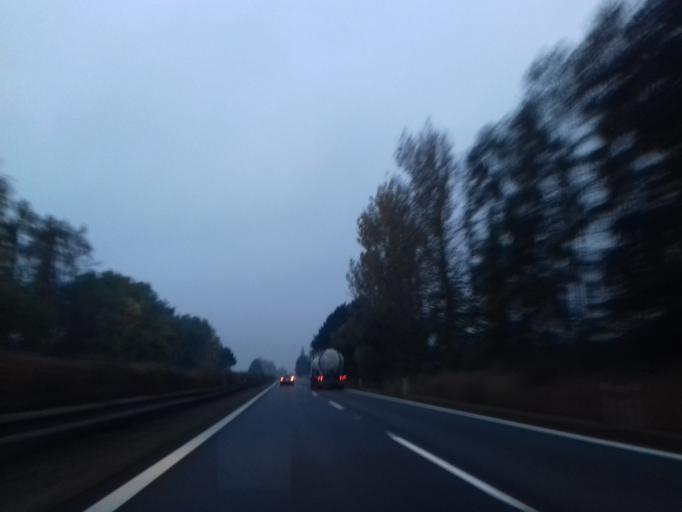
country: CZ
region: Olomoucky
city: Litovel
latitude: 49.6775
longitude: 17.0732
